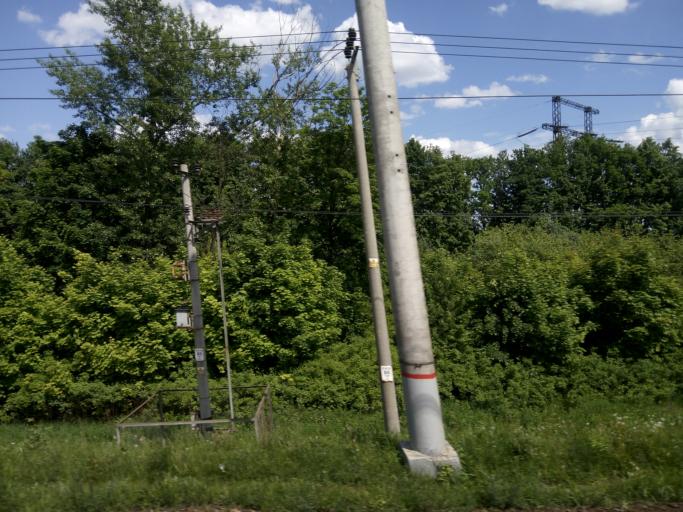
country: RU
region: Moskovskaya
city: Yam
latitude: 55.4852
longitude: 37.7349
